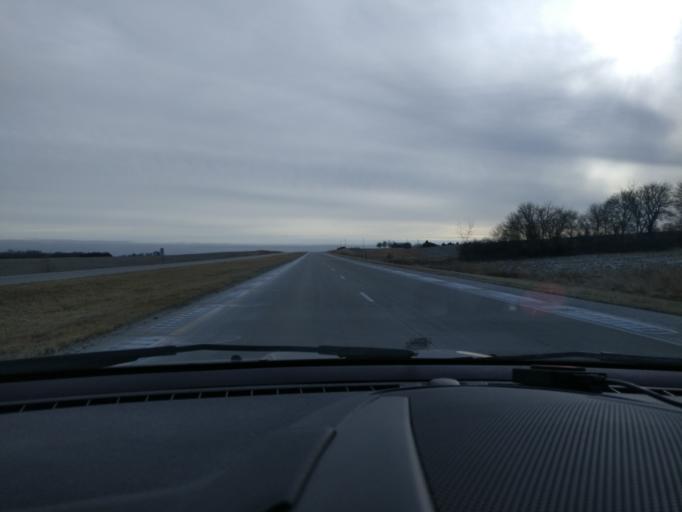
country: US
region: Nebraska
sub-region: Saunders County
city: Wahoo
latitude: 41.1448
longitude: -96.6308
